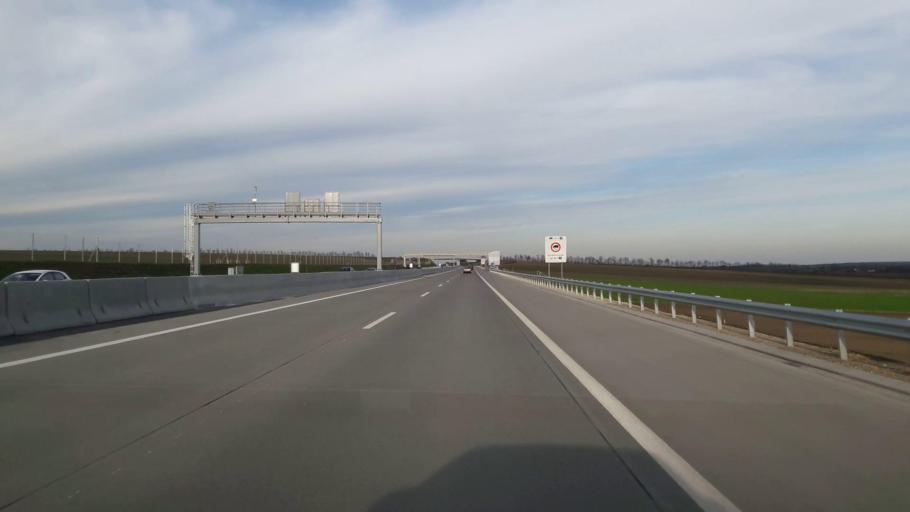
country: AT
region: Lower Austria
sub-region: Politischer Bezirk Mistelbach
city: Wilfersdorf
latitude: 48.5487
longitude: 16.6310
